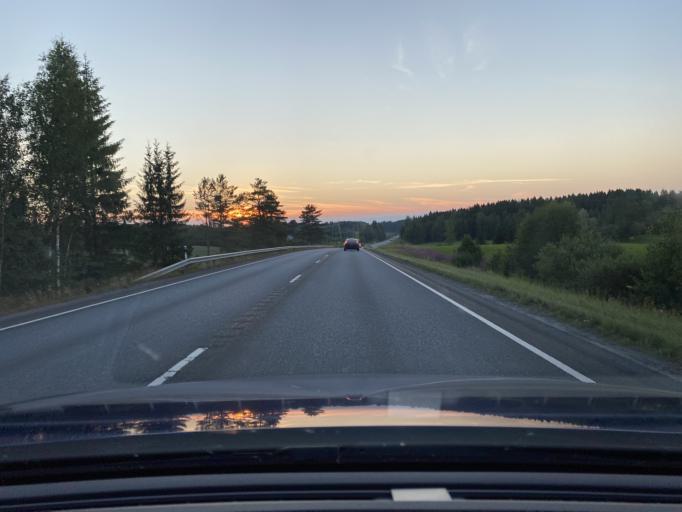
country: FI
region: Pirkanmaa
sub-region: Luoteis-Pirkanmaa
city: Ikaalinen
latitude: 61.8044
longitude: 22.9676
